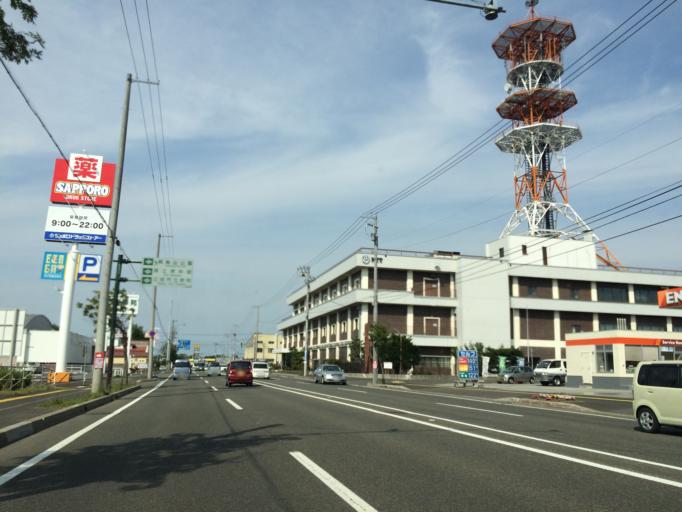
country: JP
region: Hokkaido
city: Ebetsu
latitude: 43.1097
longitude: 141.5471
